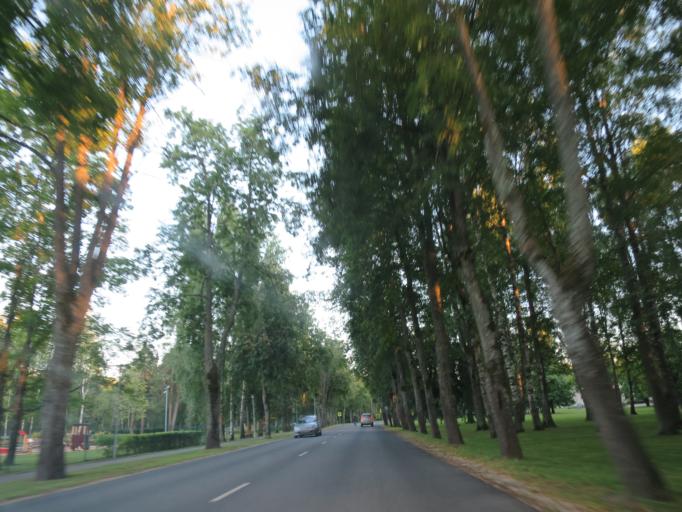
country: LV
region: Sigulda
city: Sigulda
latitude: 57.1578
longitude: 24.8536
